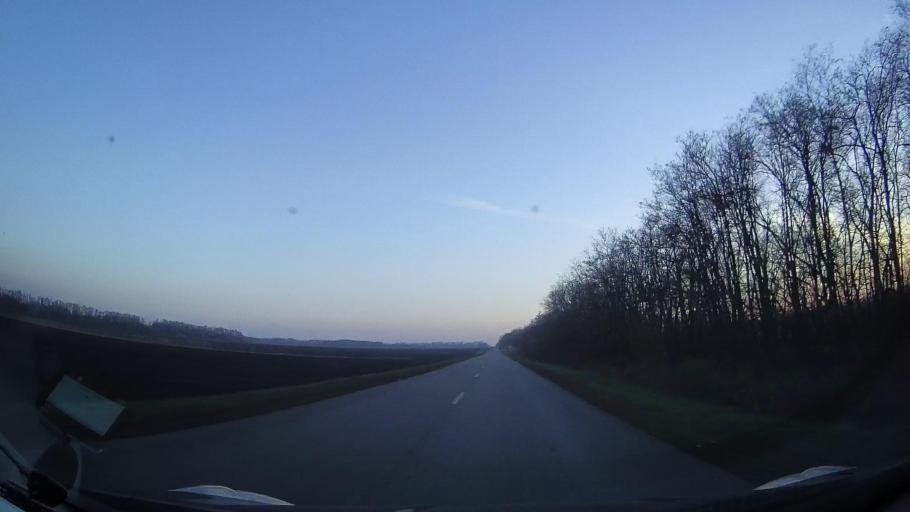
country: RU
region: Rostov
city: Zernograd
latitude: 47.0043
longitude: 40.3915
